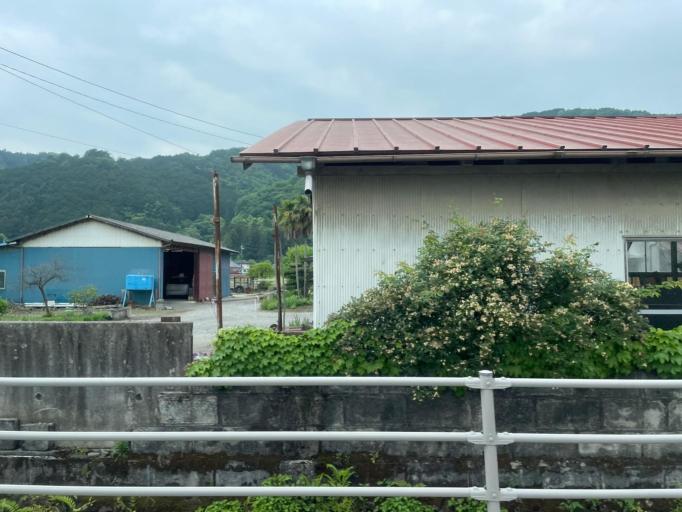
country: JP
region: Tochigi
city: Tochigi
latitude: 36.4391
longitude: 139.6558
